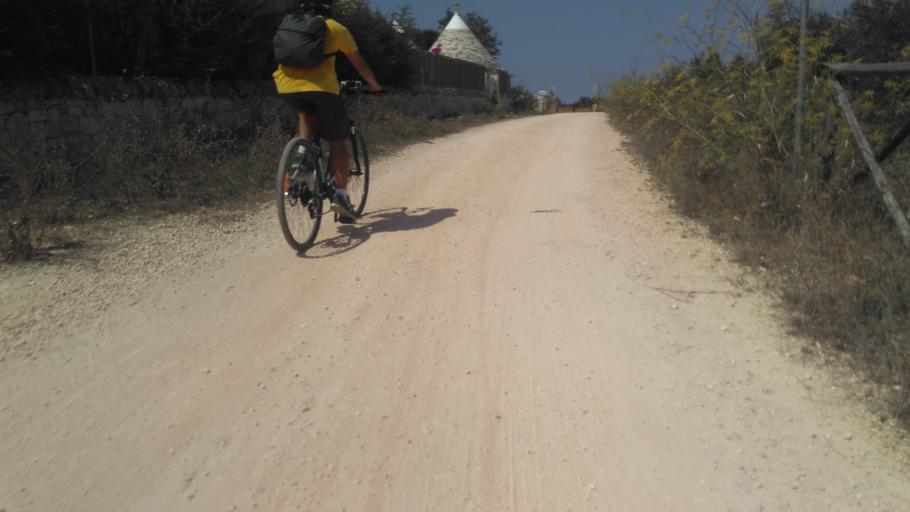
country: IT
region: Apulia
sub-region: Provincia di Brindisi
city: Cisternino
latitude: 40.6929
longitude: 17.4250
